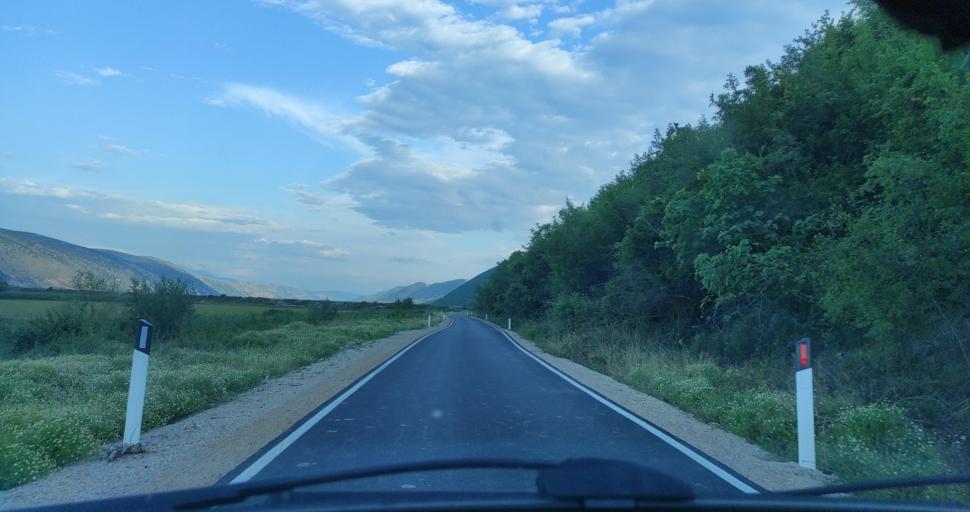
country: AL
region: Shkoder
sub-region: Rrethi i Shkodres
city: Velipoje
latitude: 41.9257
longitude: 19.4491
